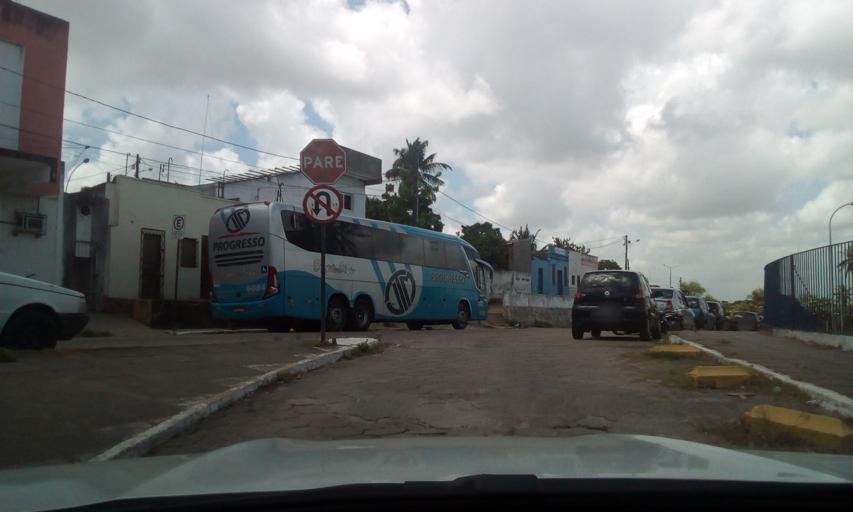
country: BR
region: Paraiba
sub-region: Joao Pessoa
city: Joao Pessoa
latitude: -7.1197
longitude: -34.8913
